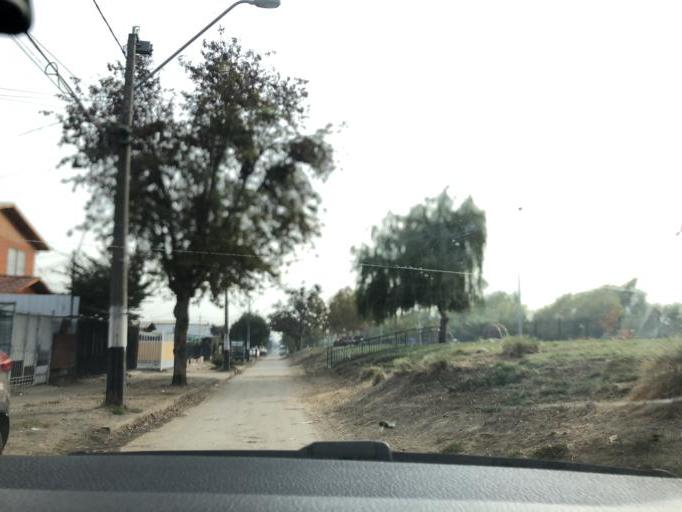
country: CL
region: Santiago Metropolitan
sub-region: Provincia de Cordillera
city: Puente Alto
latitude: -33.5627
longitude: -70.5531
